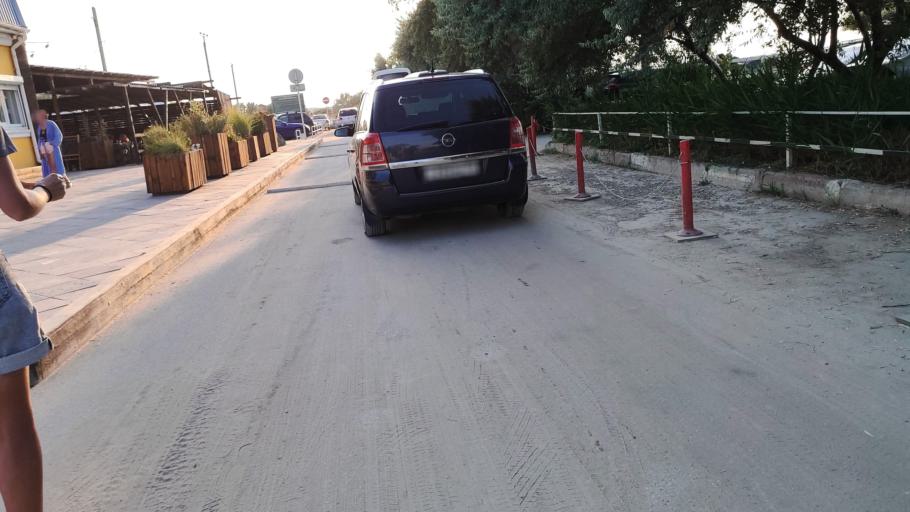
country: RU
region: Krasnodarskiy
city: Blagovetschenskaya
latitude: 45.0664
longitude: 37.0411
